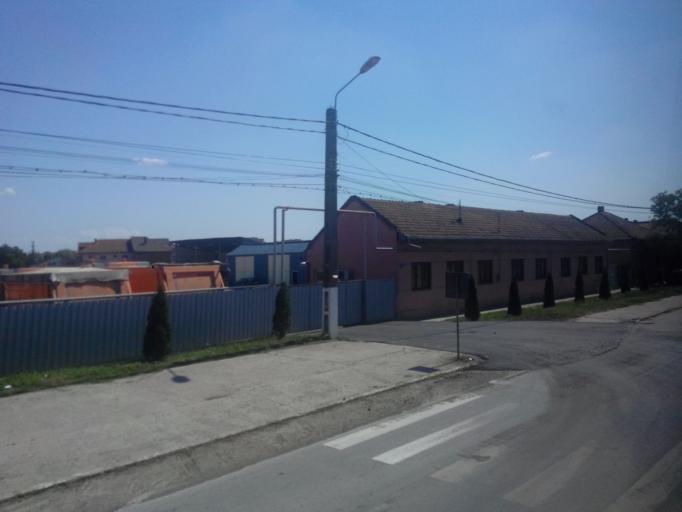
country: RO
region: Timis
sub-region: Municipiul Lugoj
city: Lugoj
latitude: 45.6959
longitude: 21.9241
